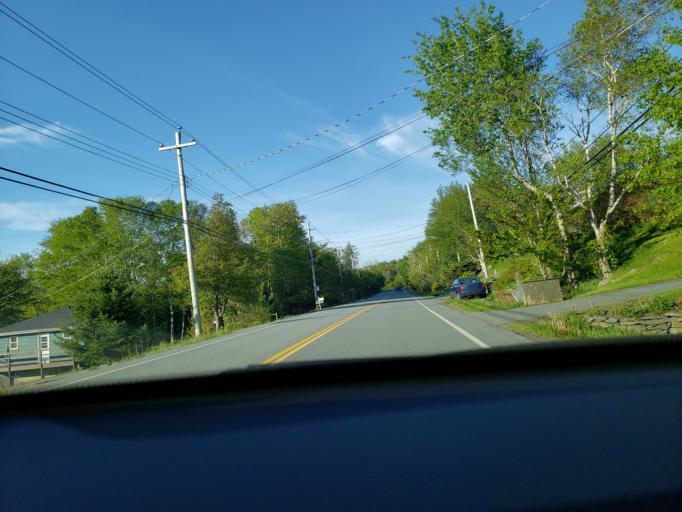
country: CA
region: Nova Scotia
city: Cole Harbour
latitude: 44.7306
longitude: -63.3935
